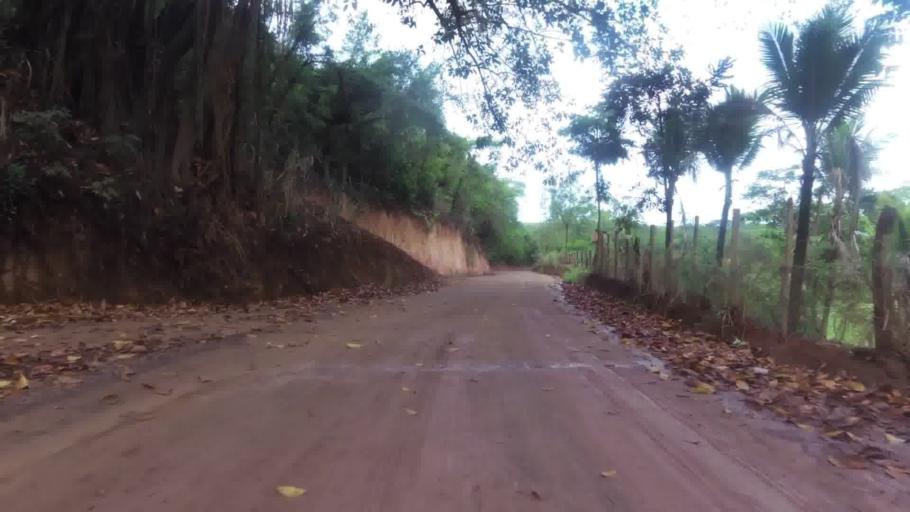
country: BR
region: Espirito Santo
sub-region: Piuma
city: Piuma
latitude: -20.7850
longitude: -40.6300
